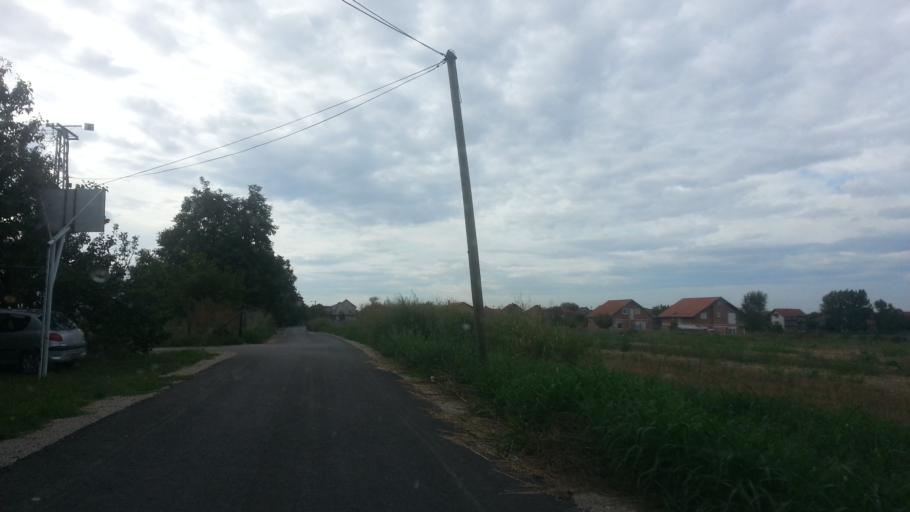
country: RS
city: Novi Banovci
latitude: 44.9625
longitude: 20.2726
